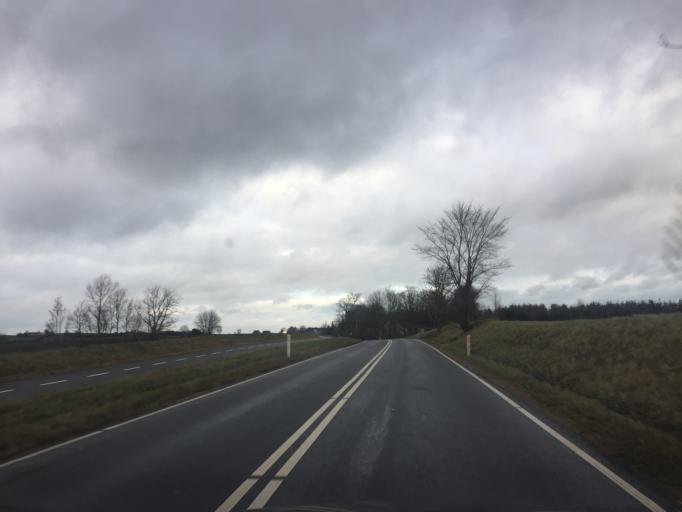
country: DK
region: Zealand
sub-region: Holbaek Kommune
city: Tollose
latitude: 55.5983
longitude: 11.6963
